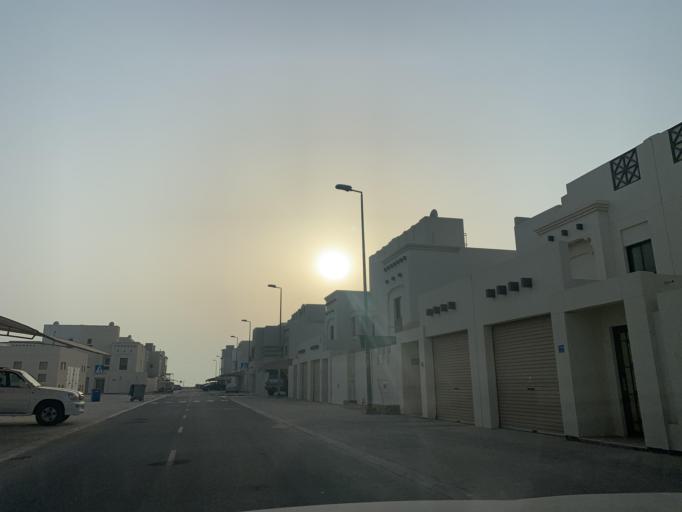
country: BH
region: Manama
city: Jidd Hafs
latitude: 26.2188
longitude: 50.4399
